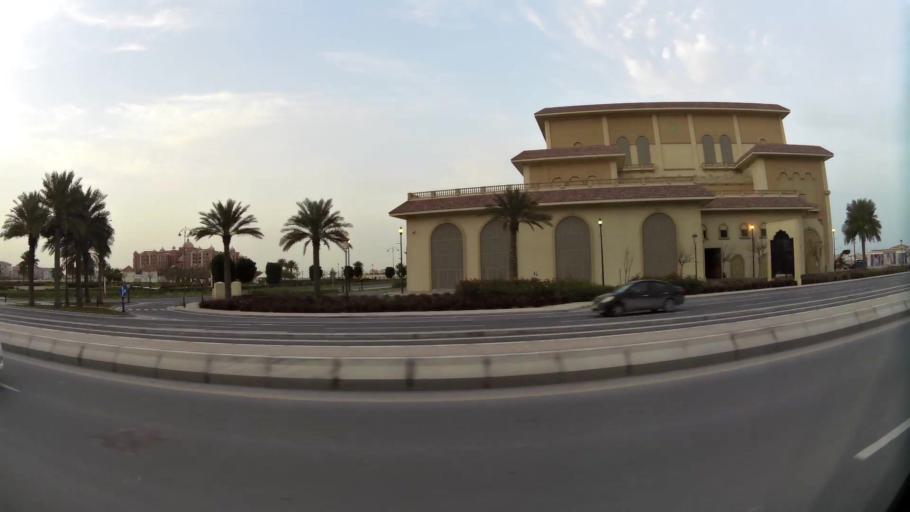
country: QA
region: Baladiyat ad Dawhah
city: Doha
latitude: 25.3711
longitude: 51.5519
